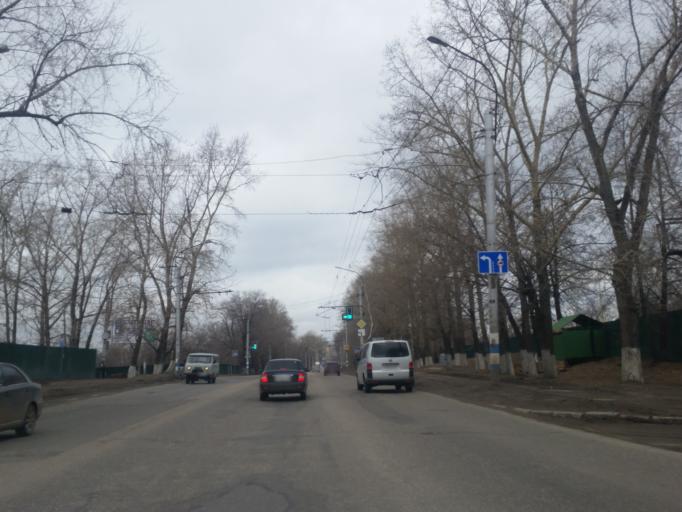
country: RU
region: Ulyanovsk
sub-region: Ulyanovskiy Rayon
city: Ulyanovsk
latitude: 54.3298
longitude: 48.4965
